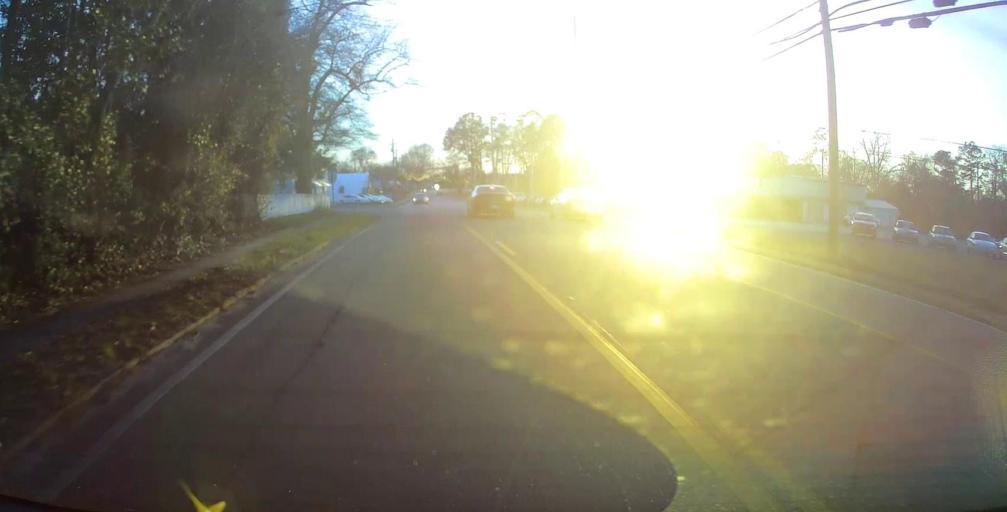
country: US
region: Georgia
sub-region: Troup County
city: La Grange
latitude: 33.0510
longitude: -85.0075
